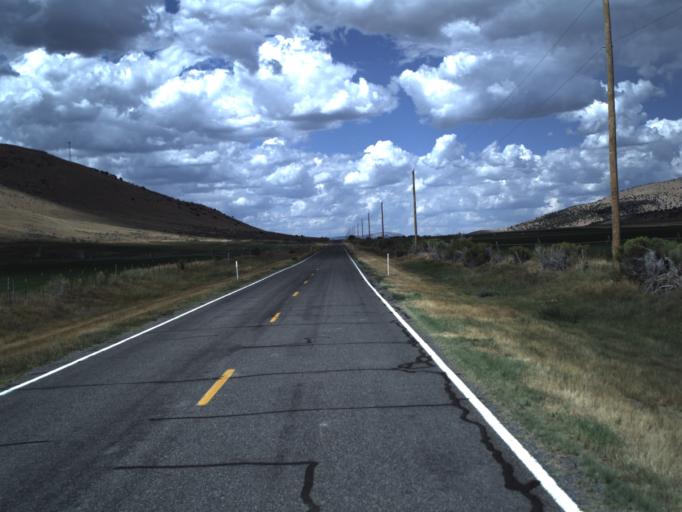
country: US
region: Utah
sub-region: Sanpete County
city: Gunnison
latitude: 39.1403
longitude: -111.7100
